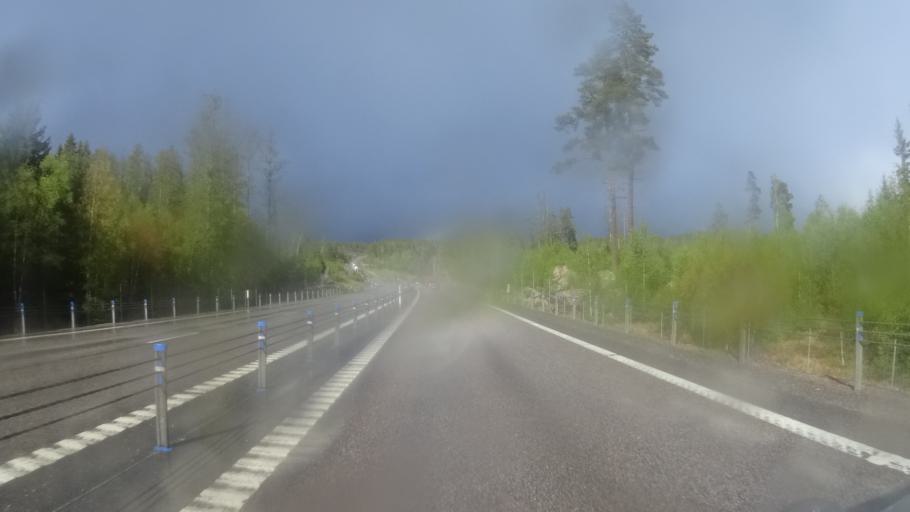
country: SE
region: OErebro
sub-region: Askersunds Kommun
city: Askersund
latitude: 58.8018
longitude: 14.8323
